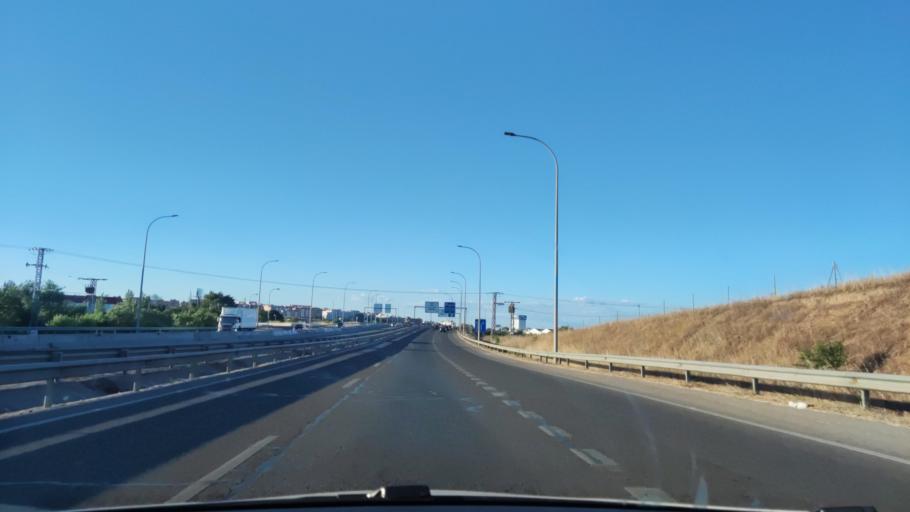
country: ES
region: Madrid
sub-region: Provincia de Madrid
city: Leganes
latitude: 40.3492
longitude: -3.7537
